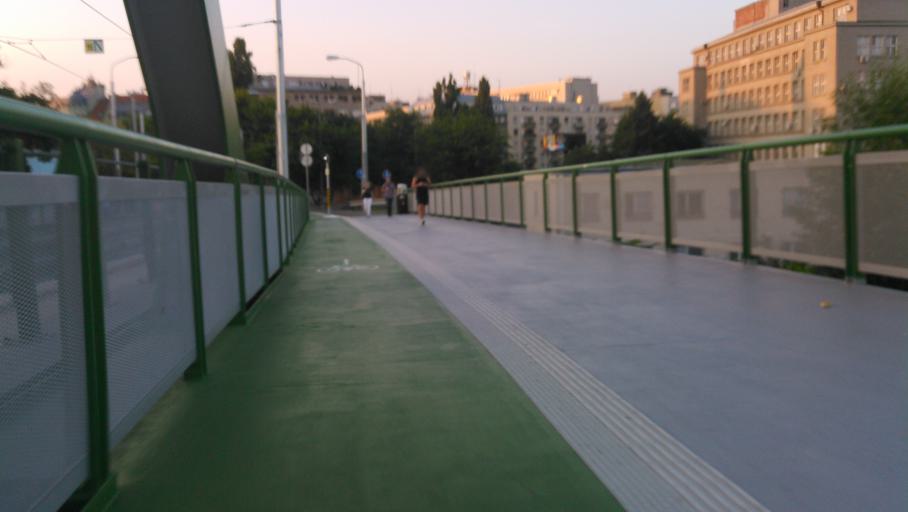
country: SK
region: Bratislavsky
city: Bratislava
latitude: 48.1397
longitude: 17.1174
